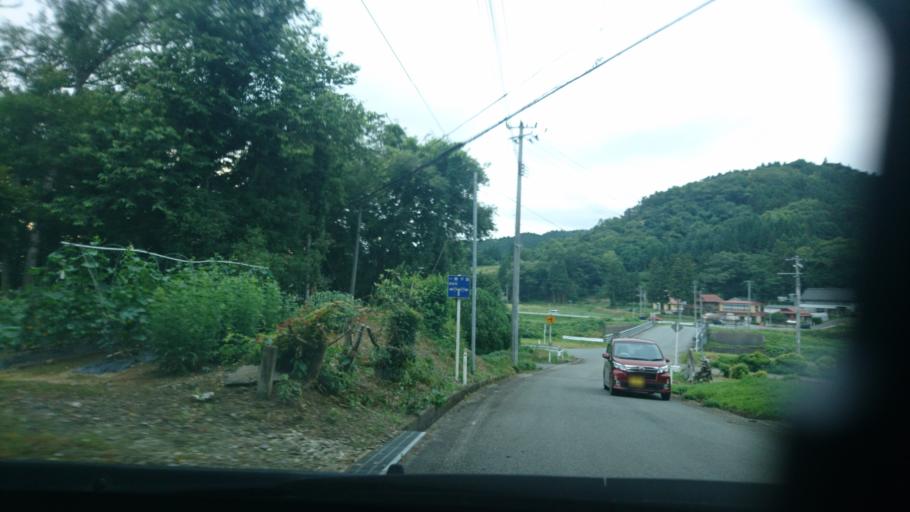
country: JP
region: Iwate
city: Ichinoseki
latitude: 38.8958
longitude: 141.3042
